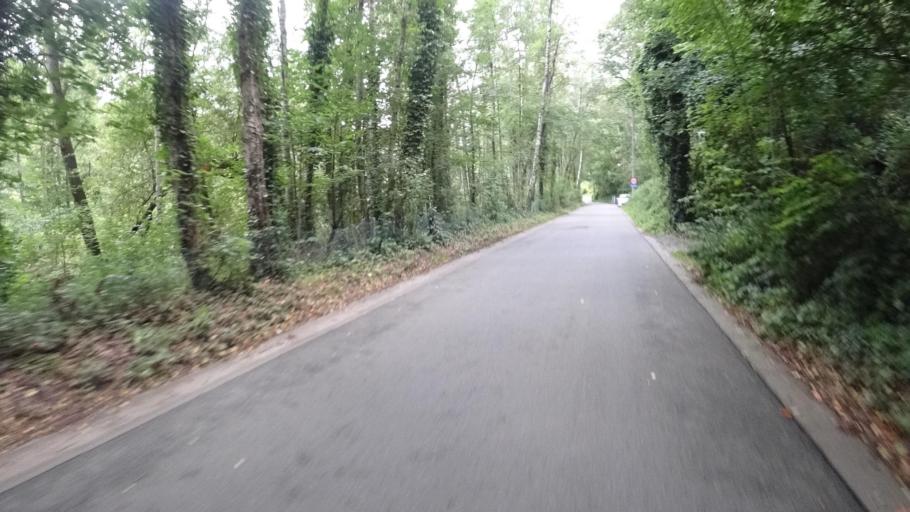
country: BE
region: Wallonia
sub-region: Province du Brabant Wallon
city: Villers-la-Ville
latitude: 50.5736
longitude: 4.5486
